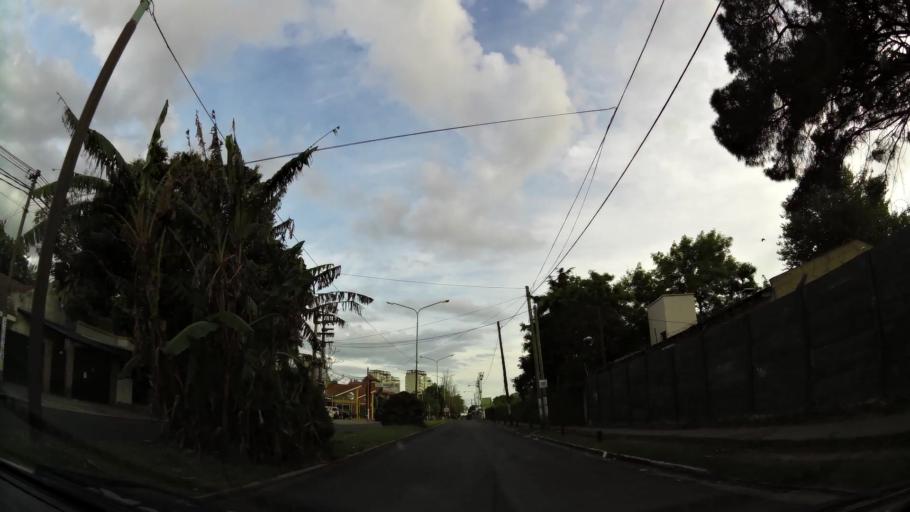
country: AR
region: Buenos Aires
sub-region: Partido de Quilmes
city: Quilmes
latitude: -34.7394
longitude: -58.2530
